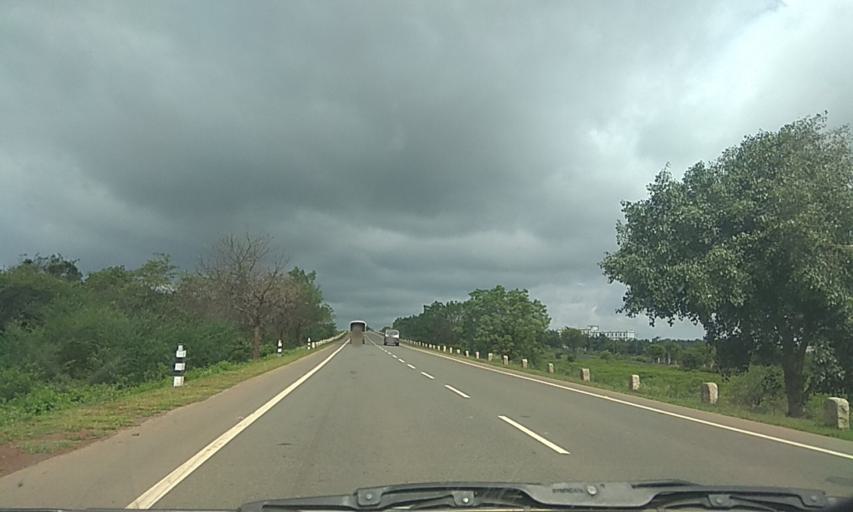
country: IN
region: Karnataka
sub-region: Dharwad
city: Hubli
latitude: 15.3406
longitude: 75.0833
